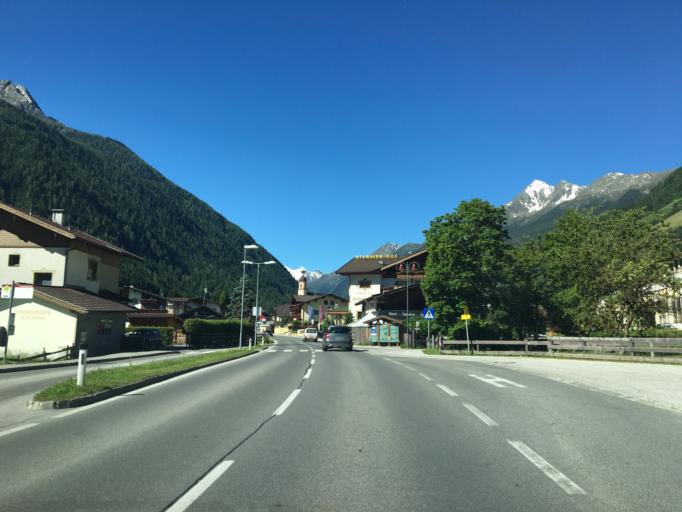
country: AT
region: Tyrol
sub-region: Politischer Bezirk Innsbruck Land
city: Neustift im Stubaital
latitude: 47.1141
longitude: 11.3120
